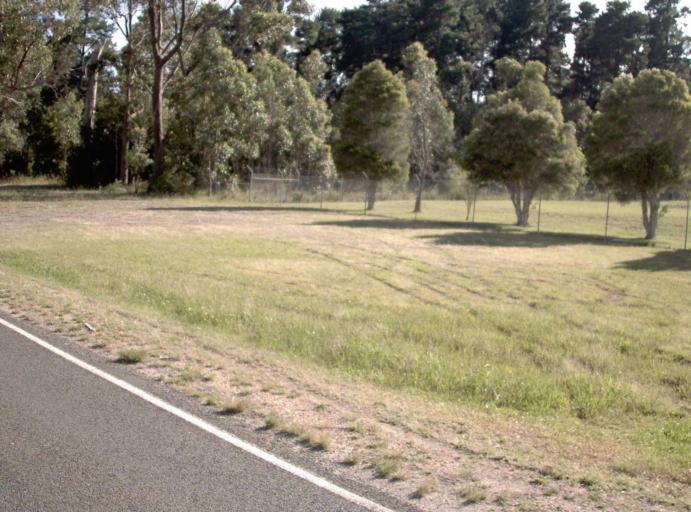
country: AU
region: Victoria
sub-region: East Gippsland
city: Lakes Entrance
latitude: -37.6918
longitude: 148.4688
